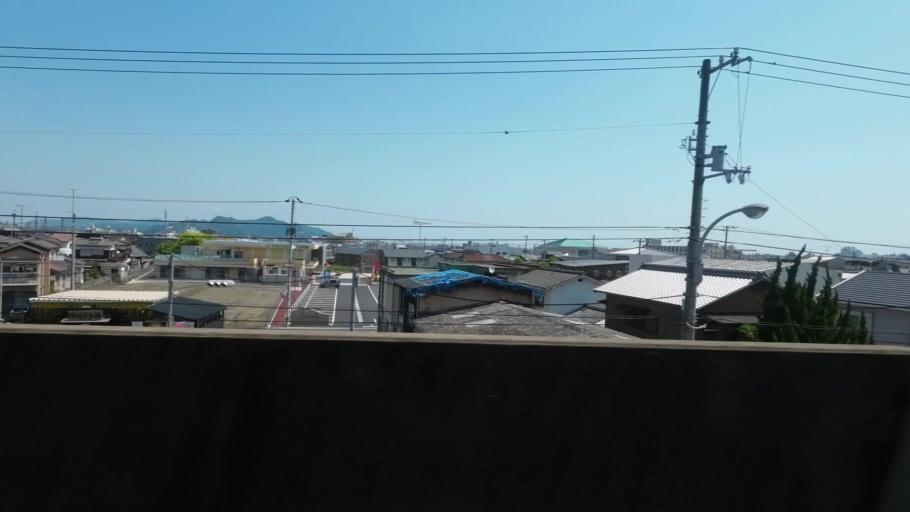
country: JP
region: Ehime
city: Hojo
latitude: 34.0710
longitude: 132.9875
